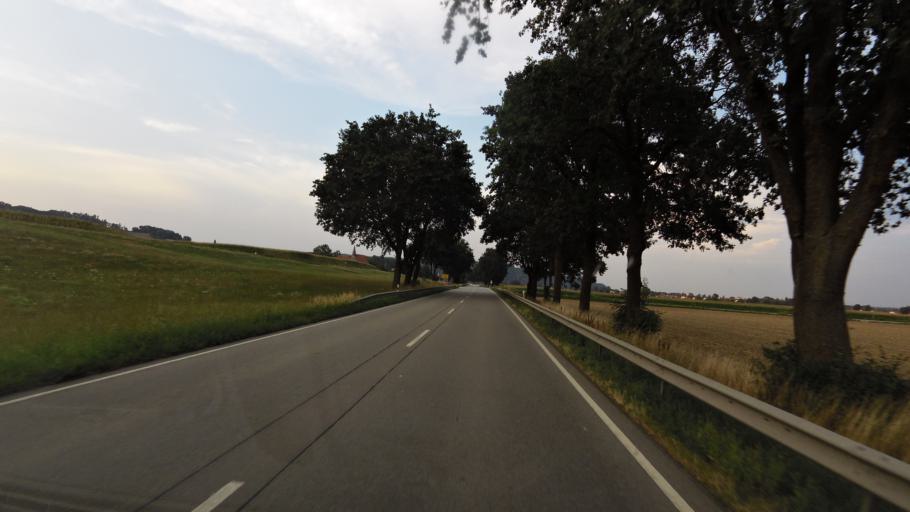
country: DE
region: Bavaria
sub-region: Lower Bavaria
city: Ering
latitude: 48.2978
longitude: 13.1237
